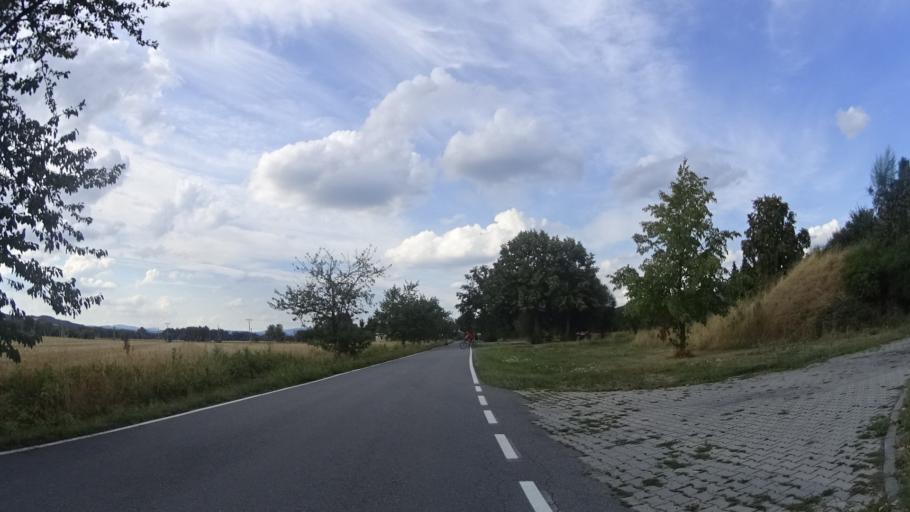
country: CZ
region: Olomoucky
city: Dubicko
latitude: 49.8227
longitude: 16.9364
